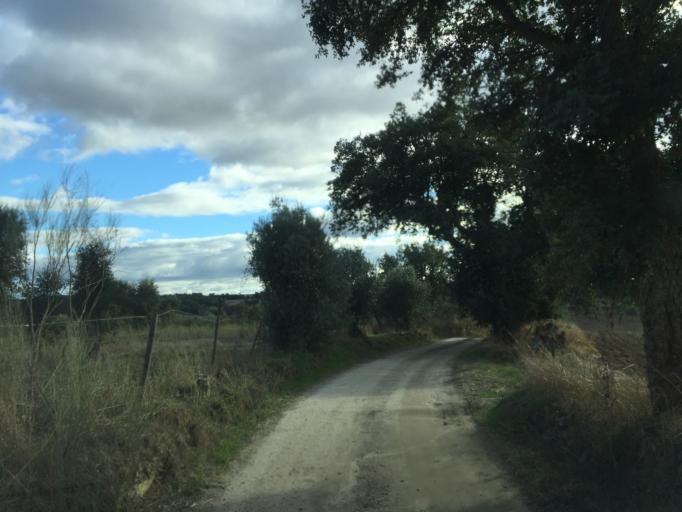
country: PT
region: Portalegre
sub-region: Alter do Chao
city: Alter do Chao
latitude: 39.2752
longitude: -7.6410
